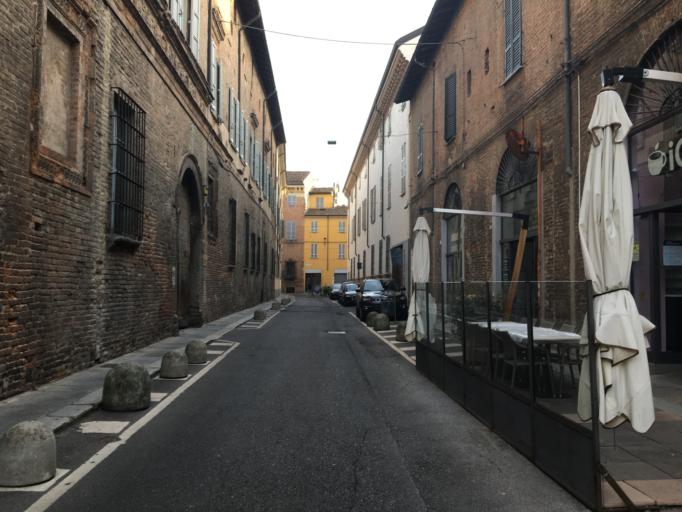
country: IT
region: Emilia-Romagna
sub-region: Provincia di Piacenza
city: Piacenza
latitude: 45.0524
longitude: 9.6988
